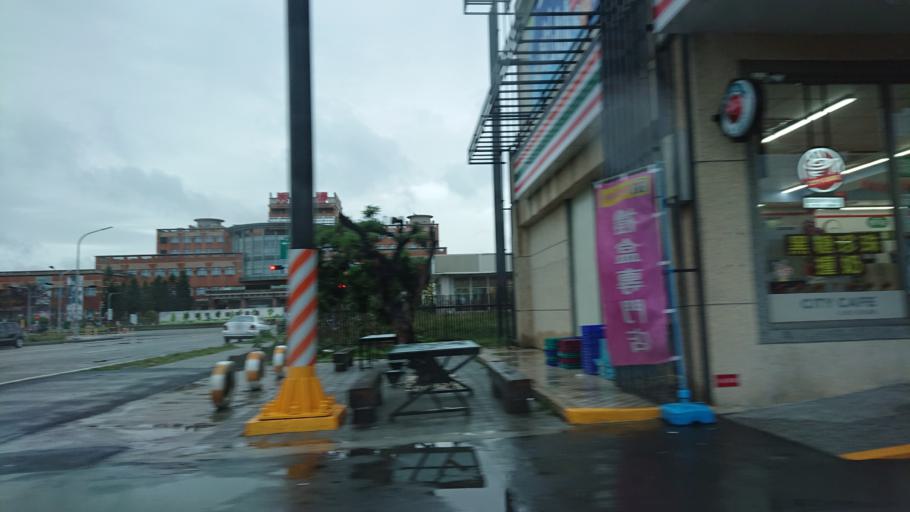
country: TW
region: Taiwan
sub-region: Changhua
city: Chang-hua
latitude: 24.0766
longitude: 120.4115
